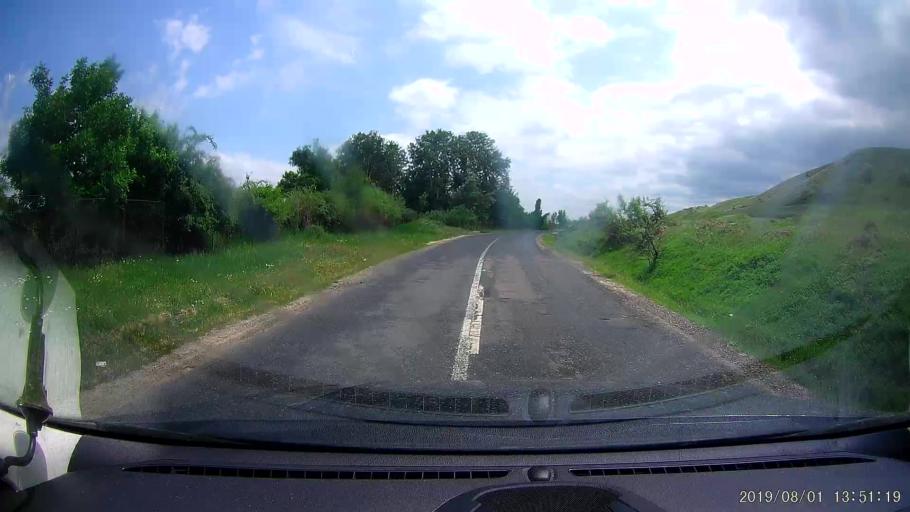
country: RO
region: Galati
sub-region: Comuna Vladesti
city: Vladesti
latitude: 45.8680
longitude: 28.0969
